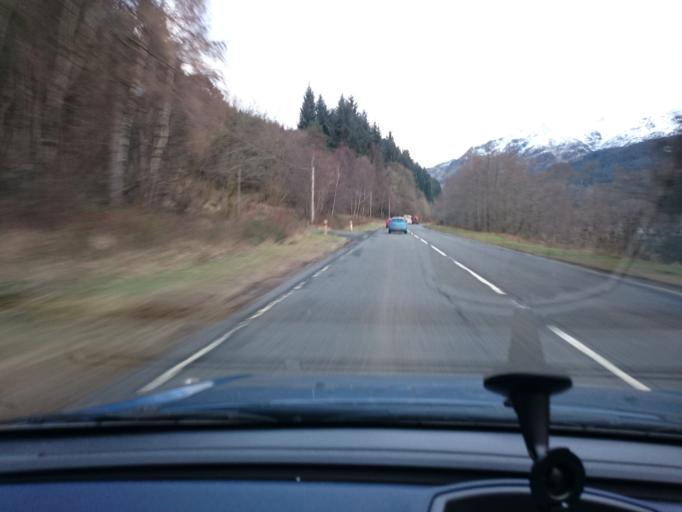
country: GB
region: Scotland
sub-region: Stirling
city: Callander
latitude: 56.3107
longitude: -4.3257
